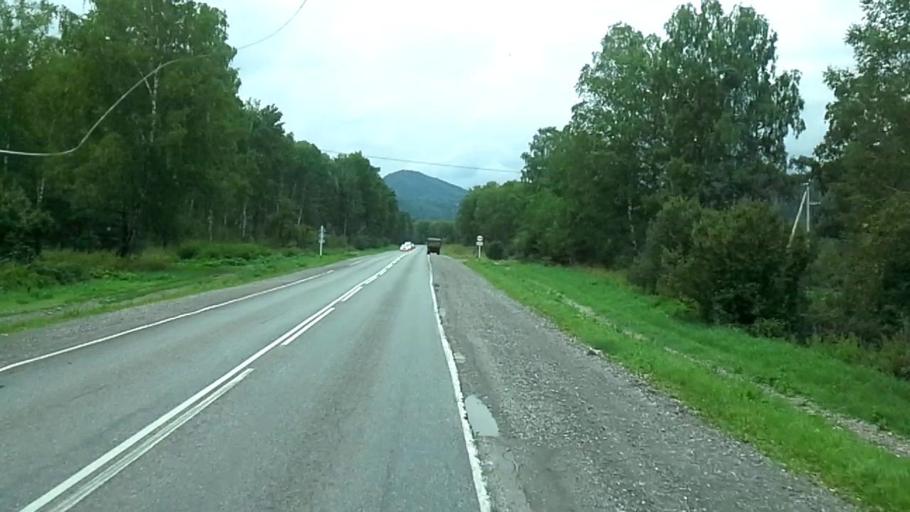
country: RU
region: Altay
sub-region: Mayminskiy Rayon
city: Manzherok
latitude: 51.8537
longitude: 85.7439
